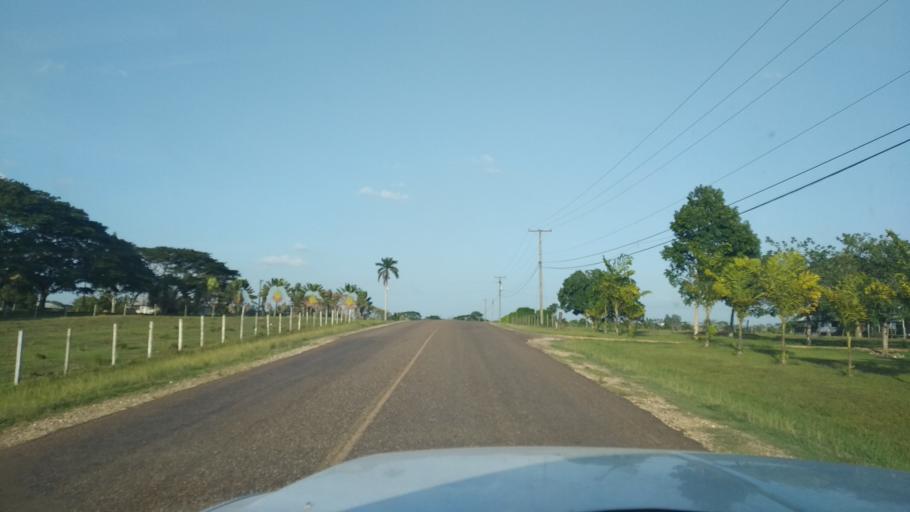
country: BZ
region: Cayo
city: San Ignacio
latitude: 17.2566
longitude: -88.9912
